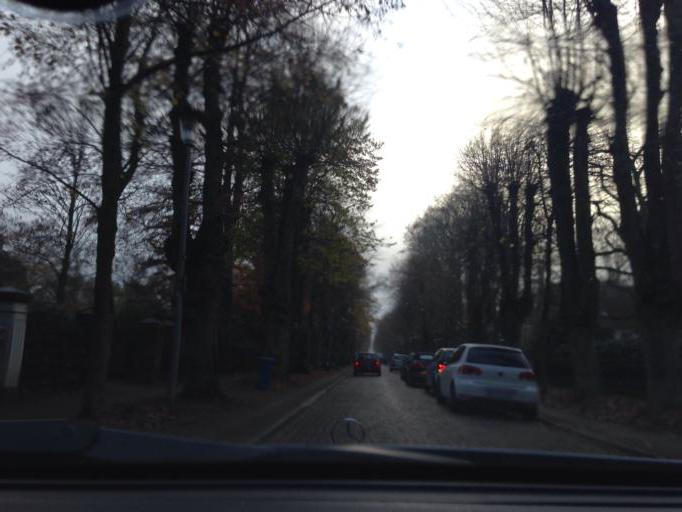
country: DE
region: Schleswig-Holstein
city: Ahrensburg
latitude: 53.6664
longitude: 10.2376
